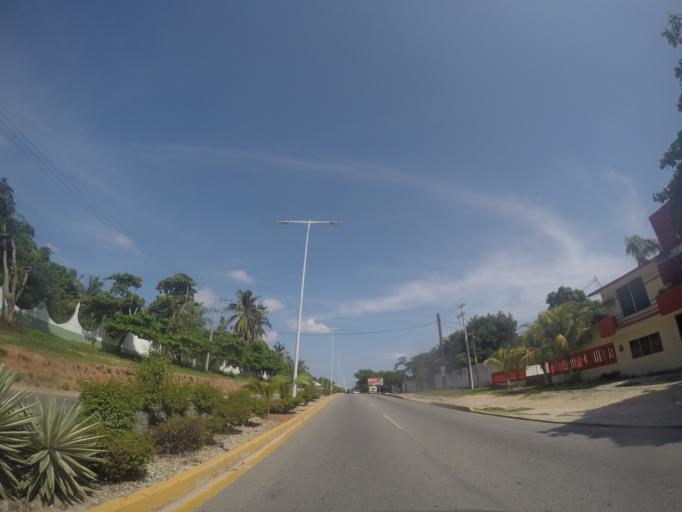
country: MX
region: Oaxaca
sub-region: Santa Maria Colotepec
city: Brisas de Zicatela
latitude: 15.8568
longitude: -97.0563
